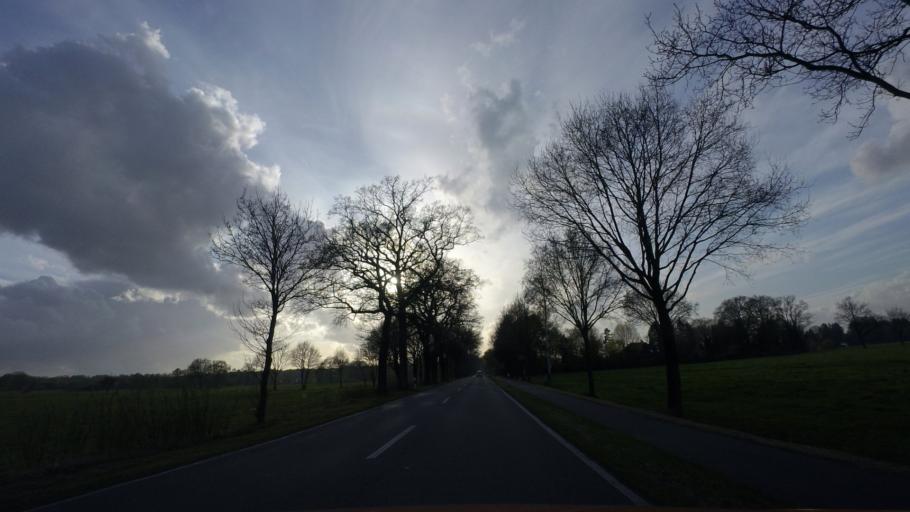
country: DE
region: Lower Saxony
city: Oldenburg
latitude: 53.1258
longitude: 8.1450
